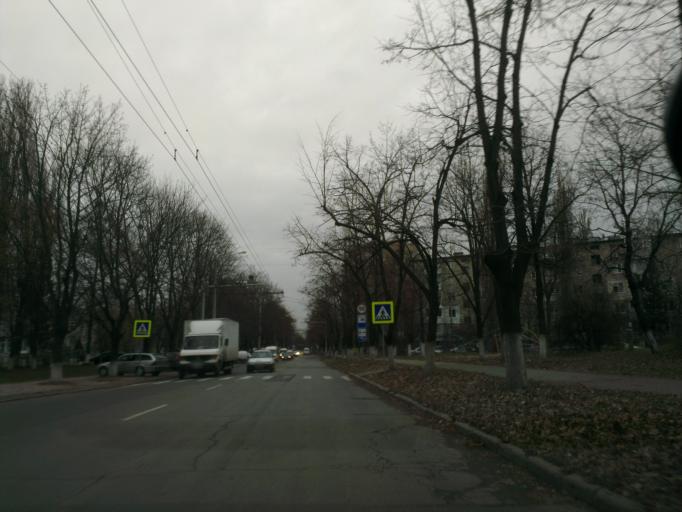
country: MD
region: Chisinau
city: Chisinau
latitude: 46.9908
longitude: 28.8455
